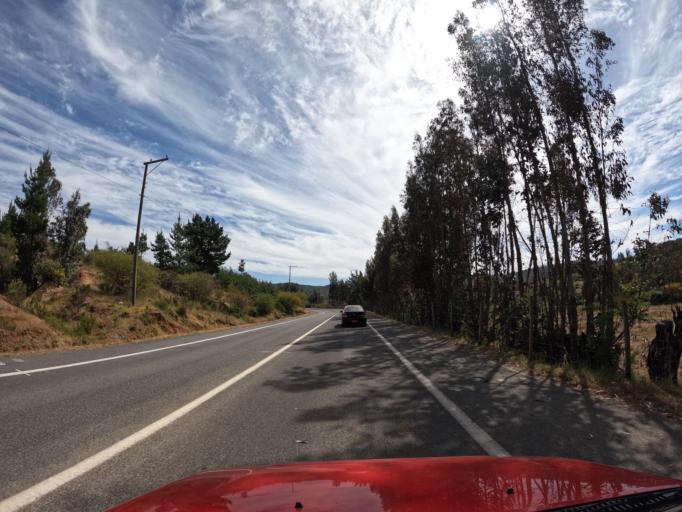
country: CL
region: Maule
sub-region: Provincia de Talca
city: Talca
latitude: -35.1309
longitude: -71.9579
